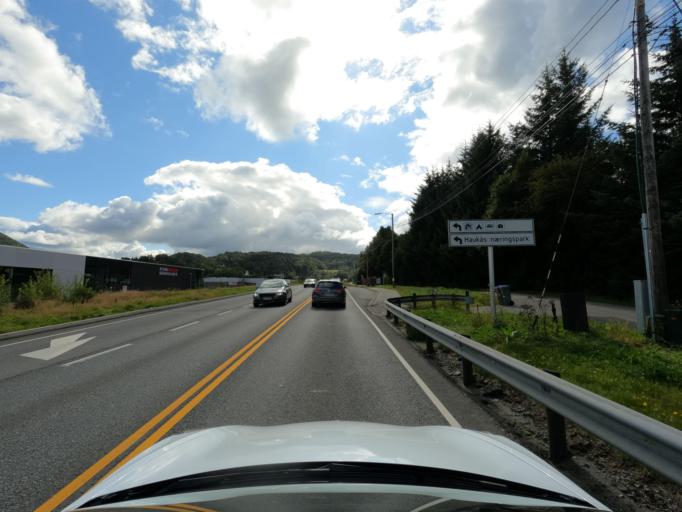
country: NO
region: Hordaland
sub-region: Bergen
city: Hylkje
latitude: 60.4873
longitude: 5.3765
